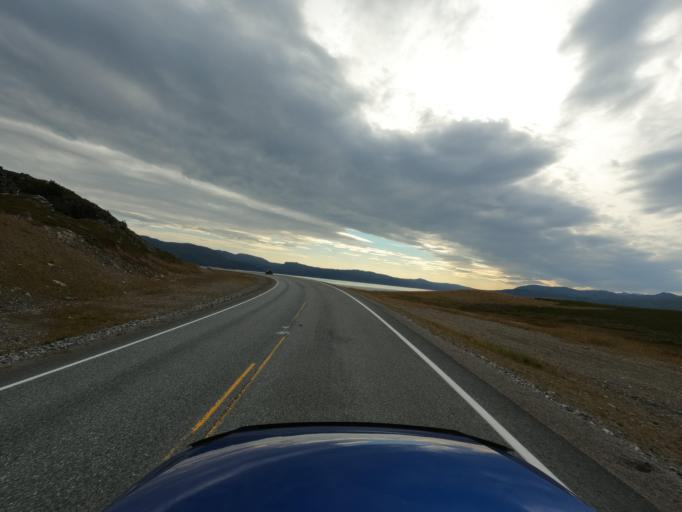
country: NO
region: Finnmark Fylke
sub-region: Hammerfest
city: Rypefjord
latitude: 70.5256
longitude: 23.7393
